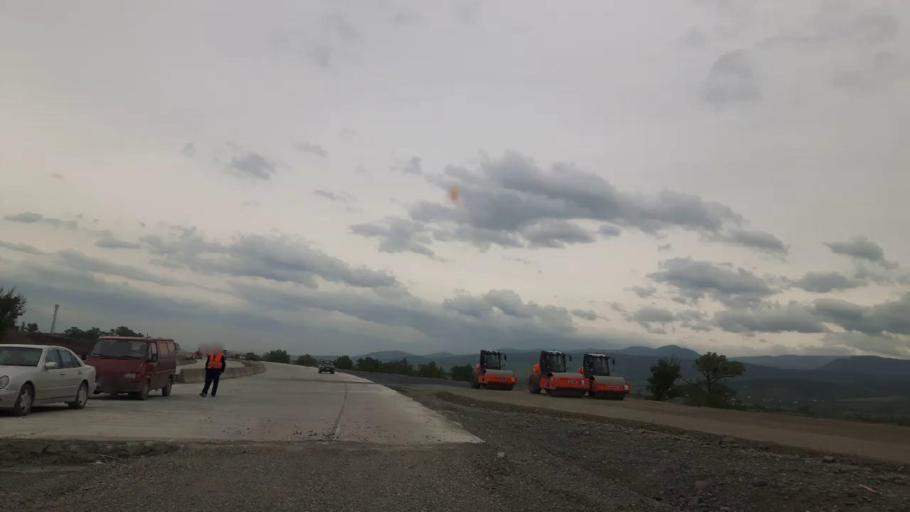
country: GE
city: Agara
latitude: 42.0114
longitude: 43.7166
